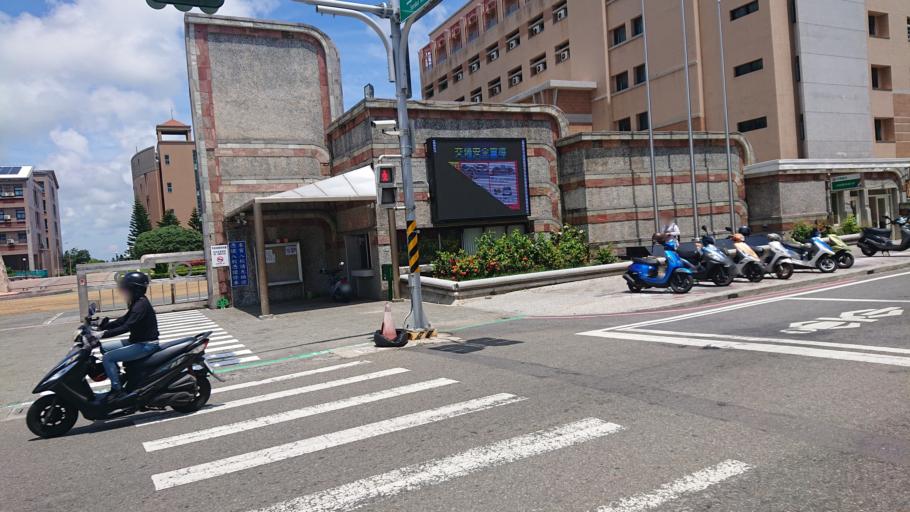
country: TW
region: Taiwan
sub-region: Penghu
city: Ma-kung
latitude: 23.5745
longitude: 119.5808
